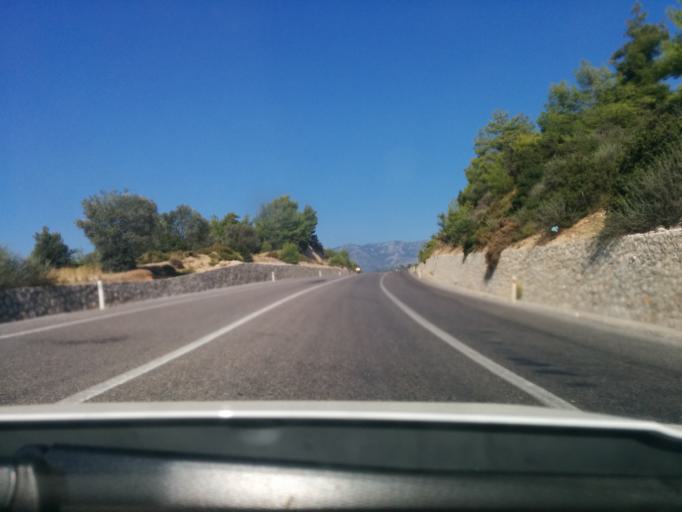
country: TR
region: Mugla
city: Esen
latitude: 36.4020
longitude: 29.3018
